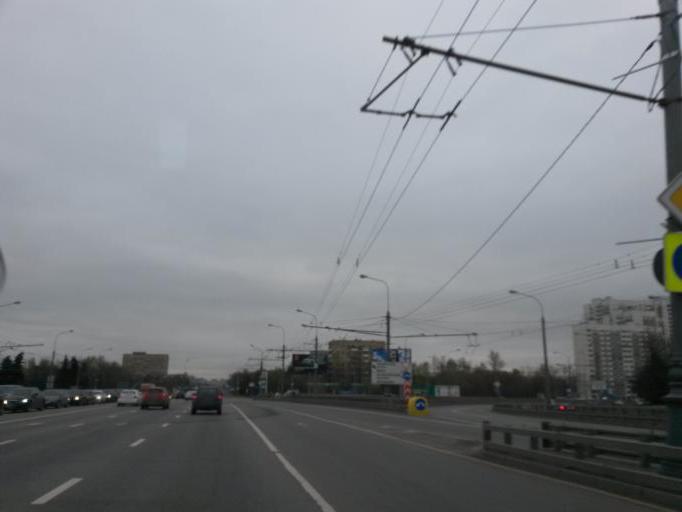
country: RU
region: Moscow
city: Tsaritsyno
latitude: 55.6517
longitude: 37.6561
